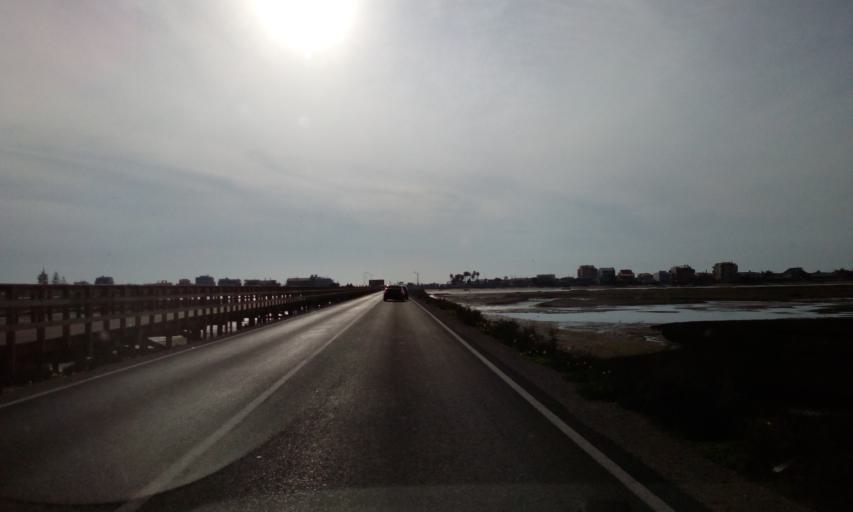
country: PT
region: Faro
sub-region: Faro
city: Faro
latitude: 37.0121
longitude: -7.9905
